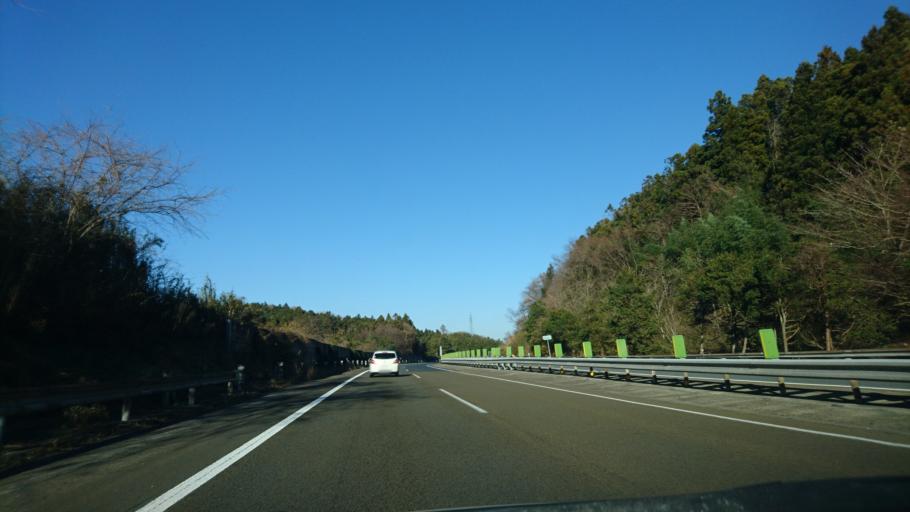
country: JP
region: Miyagi
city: Tomiya
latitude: 38.3842
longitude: 140.8928
